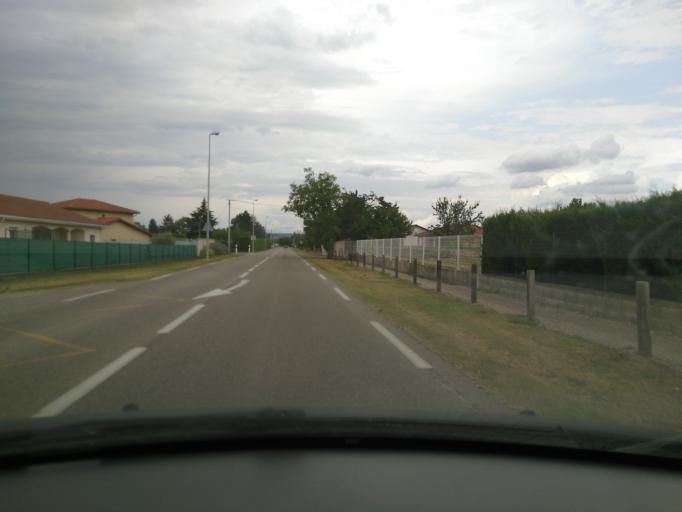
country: FR
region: Rhone-Alpes
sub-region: Departement de l'Isere
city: Beaurepaire
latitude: 45.3435
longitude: 5.0454
